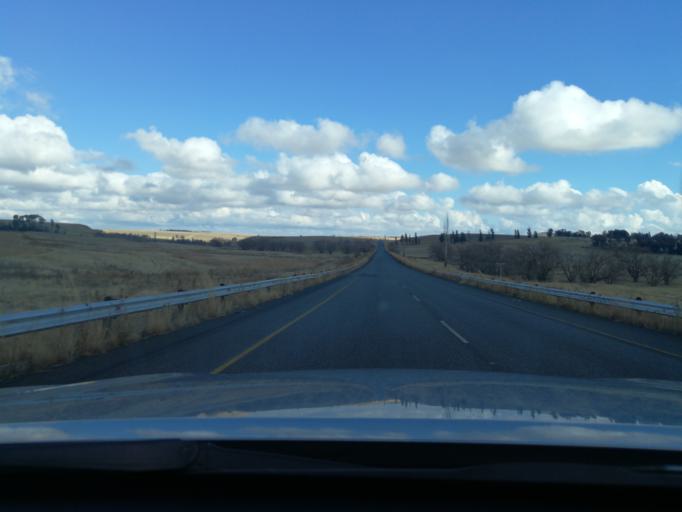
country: ZA
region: Orange Free State
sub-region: Thabo Mofutsanyana District Municipality
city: Reitz
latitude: -27.9415
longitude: 28.3850
